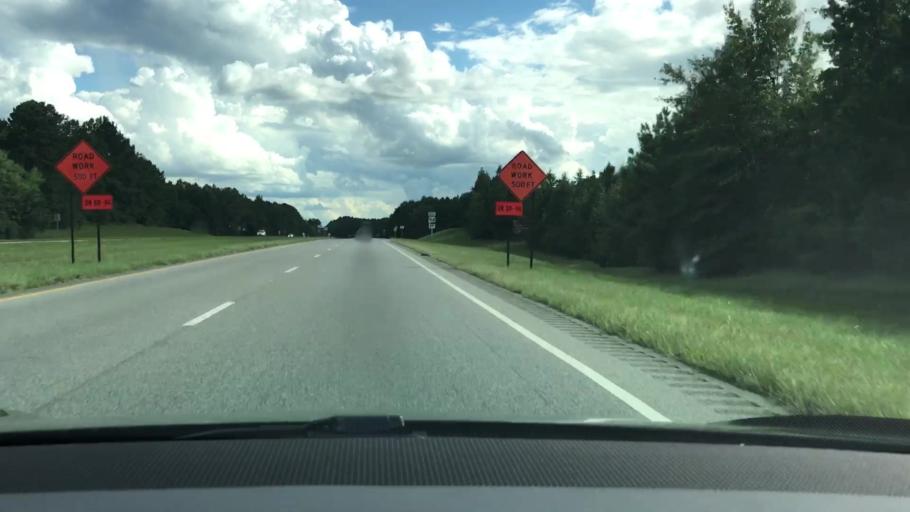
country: US
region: Alabama
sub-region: Pike County
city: Troy
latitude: 31.9809
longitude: -86.0270
